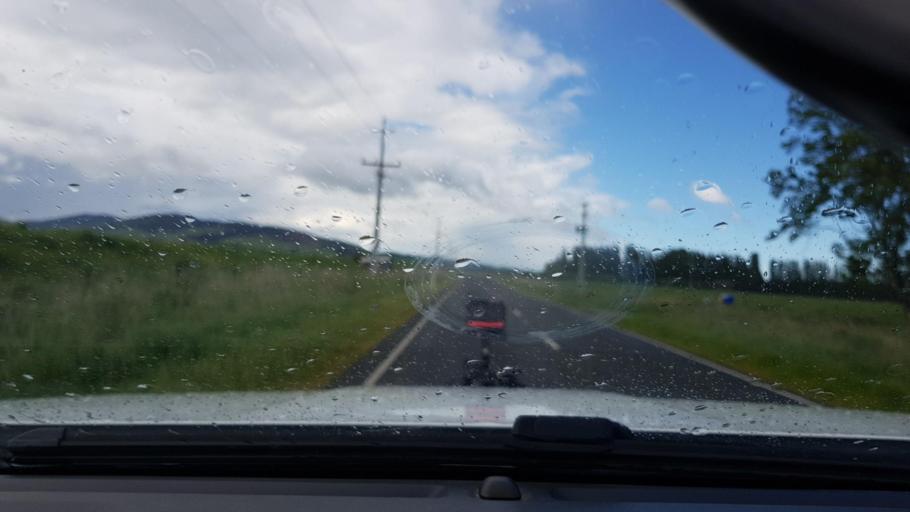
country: NZ
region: Southland
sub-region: Southland District
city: Winton
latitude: -45.8096
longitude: 168.3767
